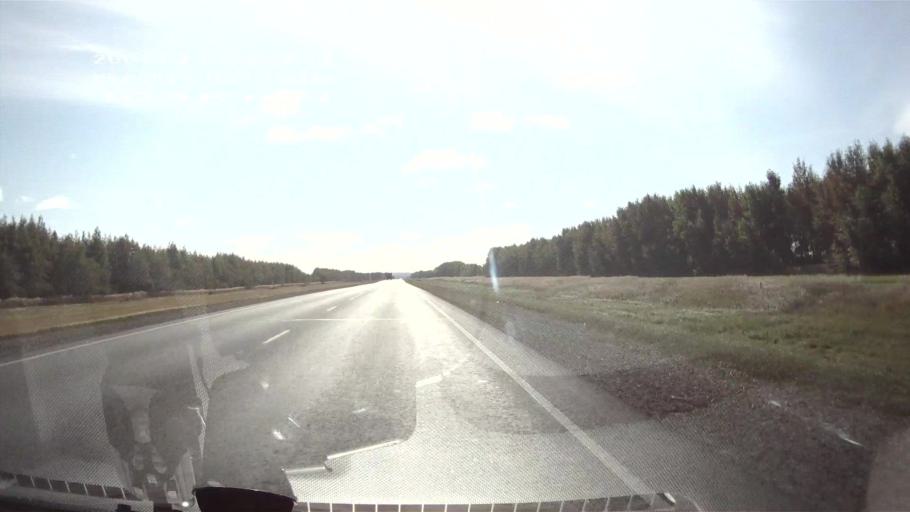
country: RU
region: Ulyanovsk
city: Tsil'na
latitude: 54.5630
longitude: 47.9219
